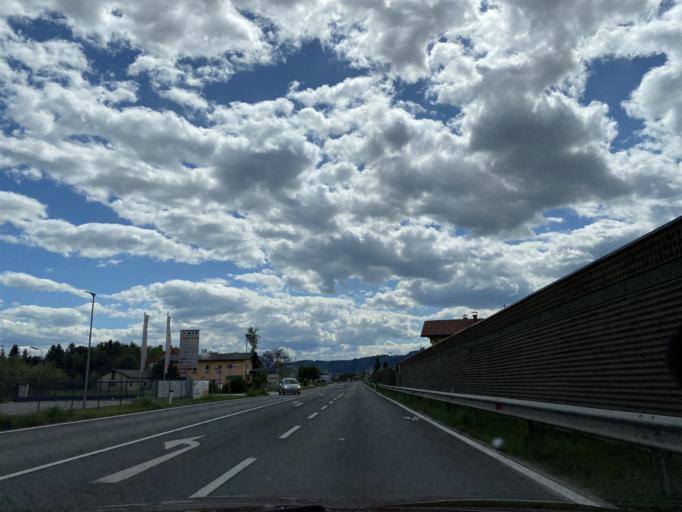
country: AT
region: Carinthia
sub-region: Politischer Bezirk Wolfsberg
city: Wolfsberg
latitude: 46.8136
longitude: 14.8340
